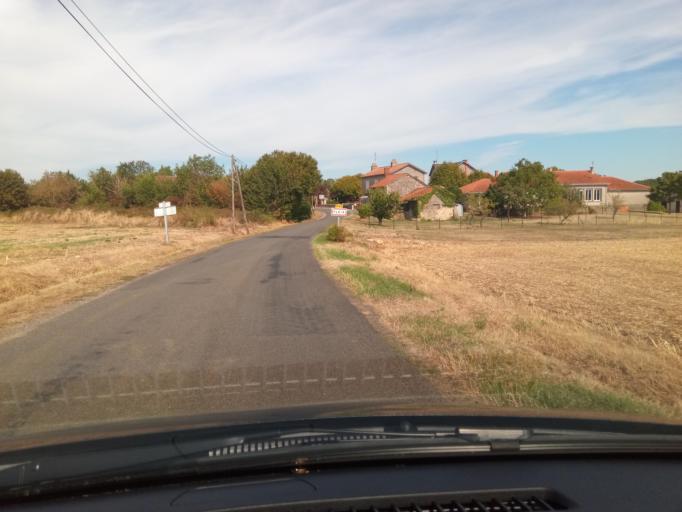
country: FR
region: Poitou-Charentes
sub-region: Departement de la Vienne
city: Chauvigny
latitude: 46.5533
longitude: 0.7442
